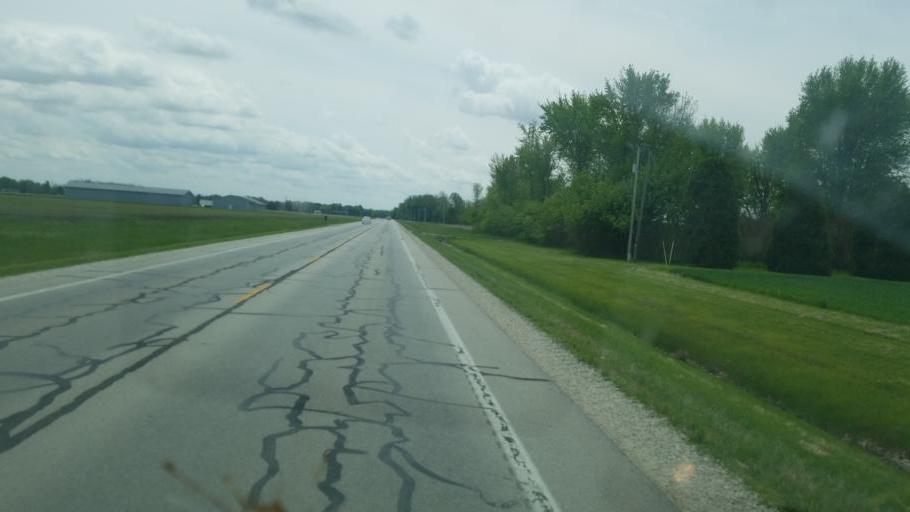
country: US
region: Ohio
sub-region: Sandusky County
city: Ballville
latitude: 41.3102
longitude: -83.1684
